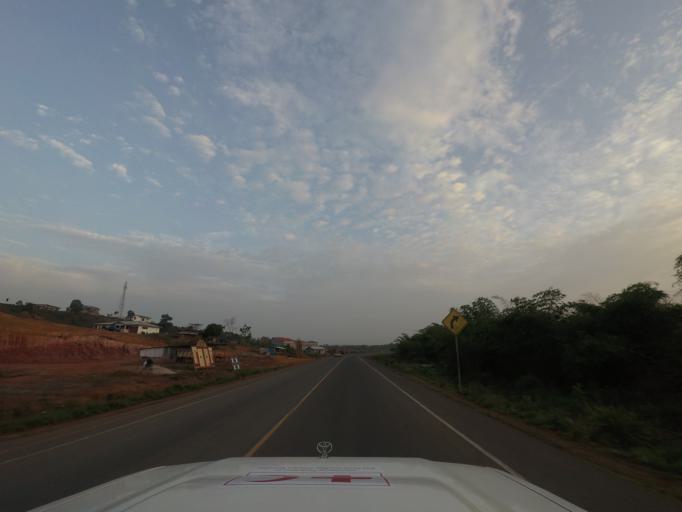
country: LR
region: Montserrado
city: Bensonville City
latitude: 6.3367
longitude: -10.6590
